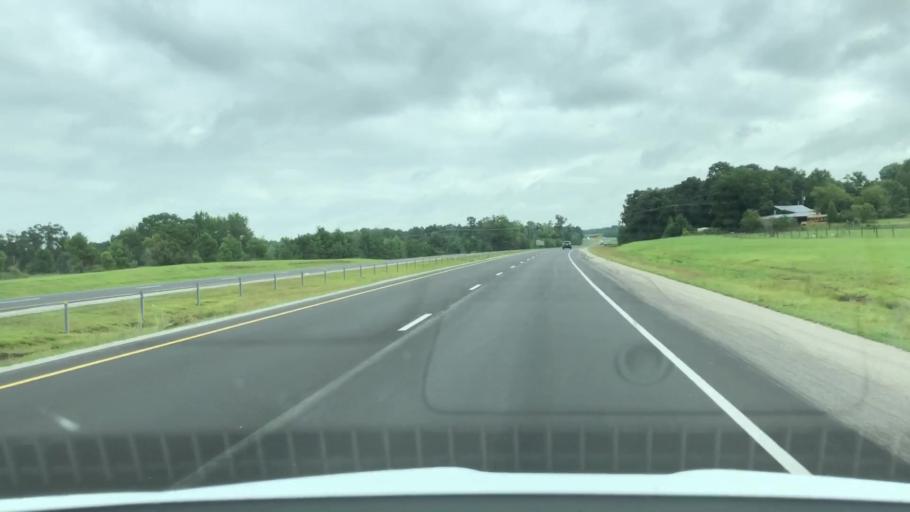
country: US
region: North Carolina
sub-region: Wilson County
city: Lucama
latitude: 35.6330
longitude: -77.9716
